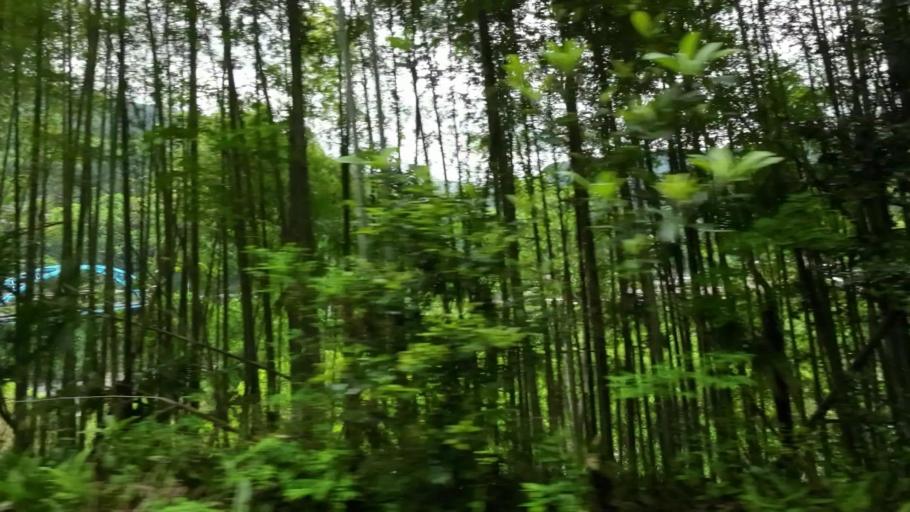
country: JP
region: Tokushima
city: Ikedacho
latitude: 33.9706
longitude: 133.7753
